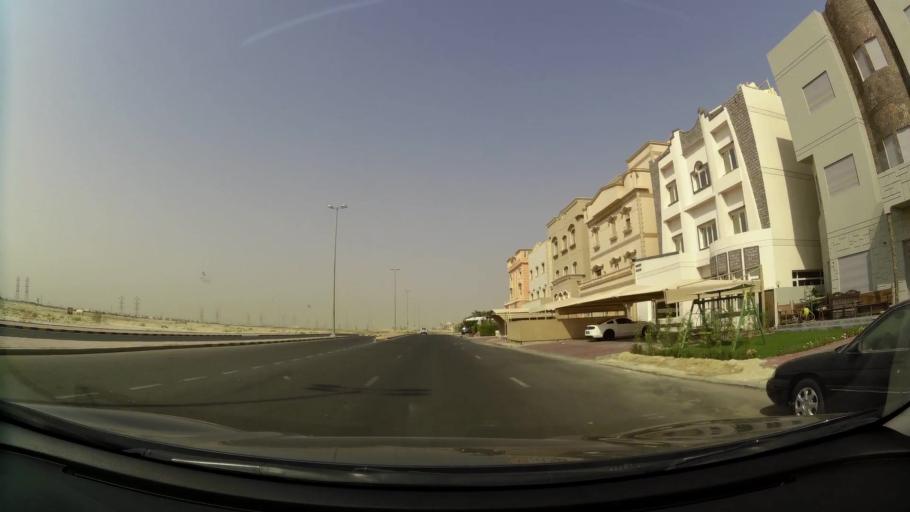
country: KW
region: Muhafazat al Jahra'
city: Al Jahra'
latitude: 29.3274
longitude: 47.7696
